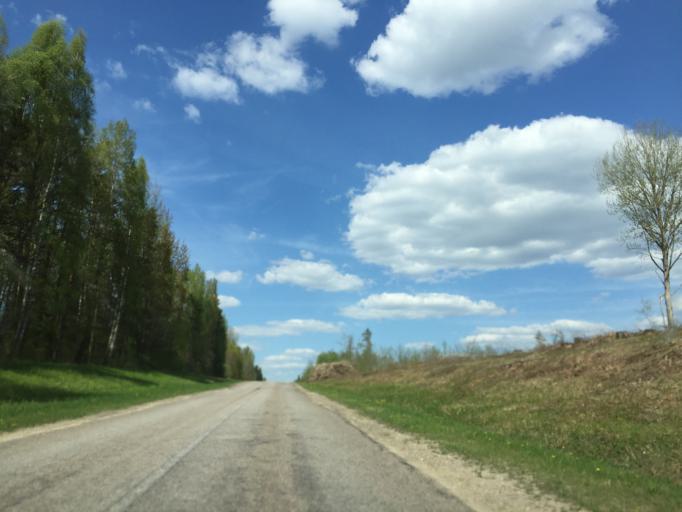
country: LV
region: Limbazu Rajons
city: Limbazi
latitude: 57.4094
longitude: 24.6934
